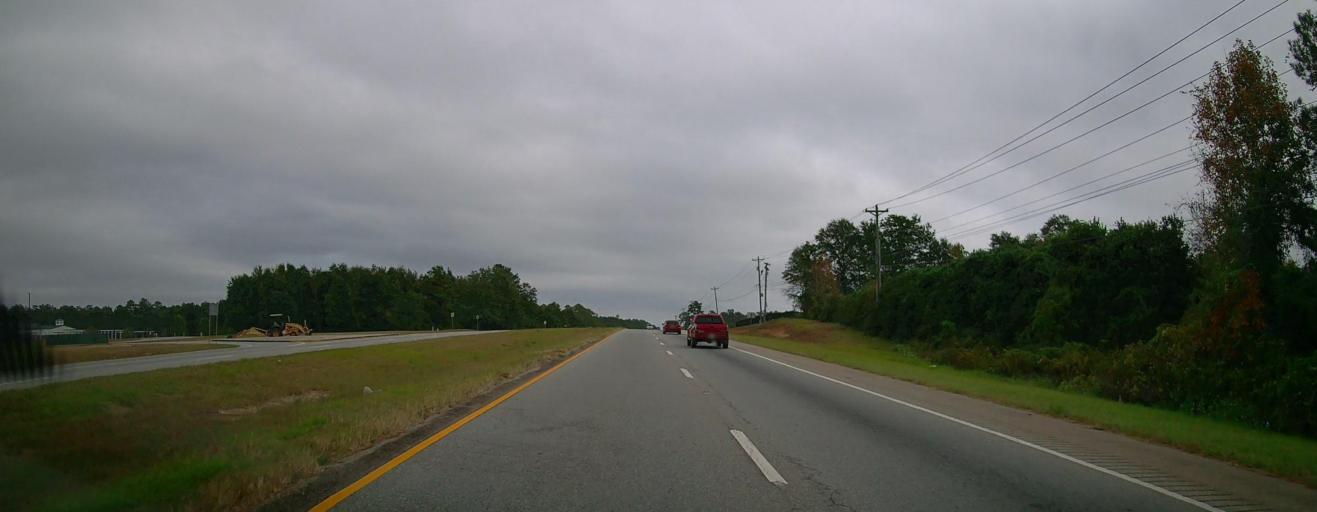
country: US
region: Georgia
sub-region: Thomas County
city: Thomasville
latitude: 30.8748
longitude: -83.9700
